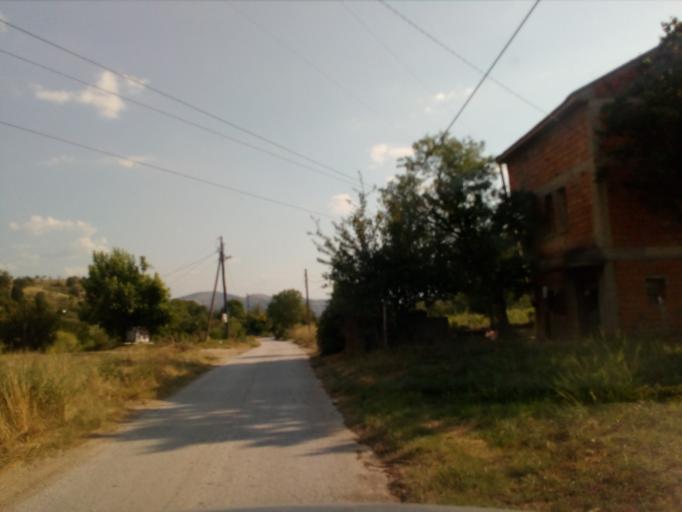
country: MK
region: Veles
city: Veles
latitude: 41.7508
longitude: 21.7941
